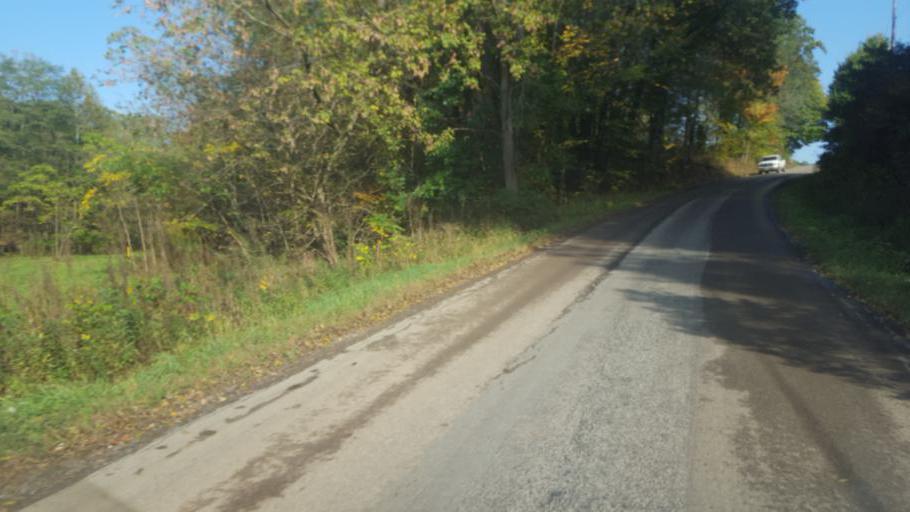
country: US
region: Ohio
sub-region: Wayne County
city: Apple Creek
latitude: 40.6754
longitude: -81.8627
